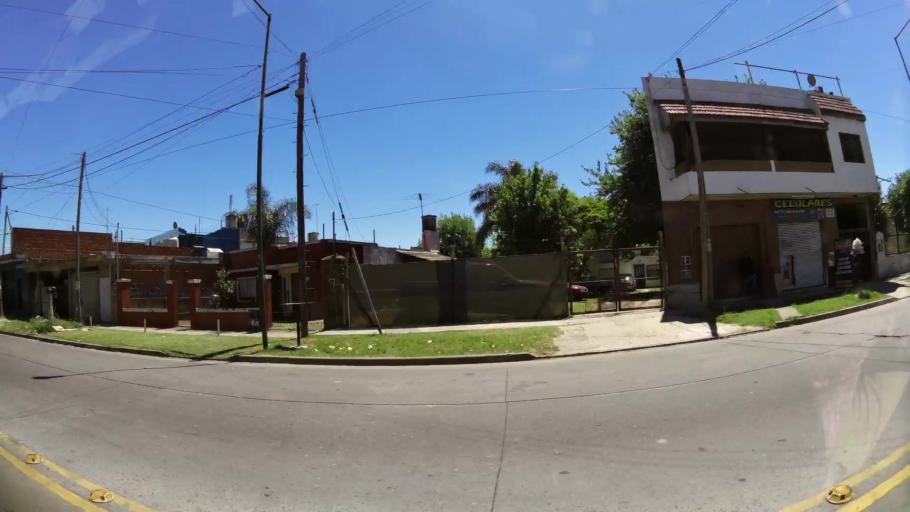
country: AR
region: Buenos Aires
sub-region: Partido de Tigre
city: Tigre
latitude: -34.5029
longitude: -58.5849
